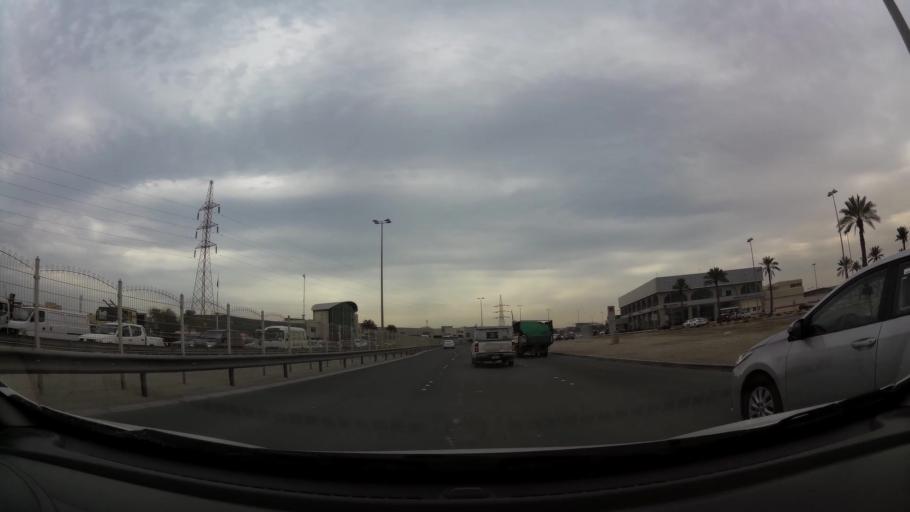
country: BH
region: Northern
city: Sitrah
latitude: 26.1707
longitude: 50.6024
